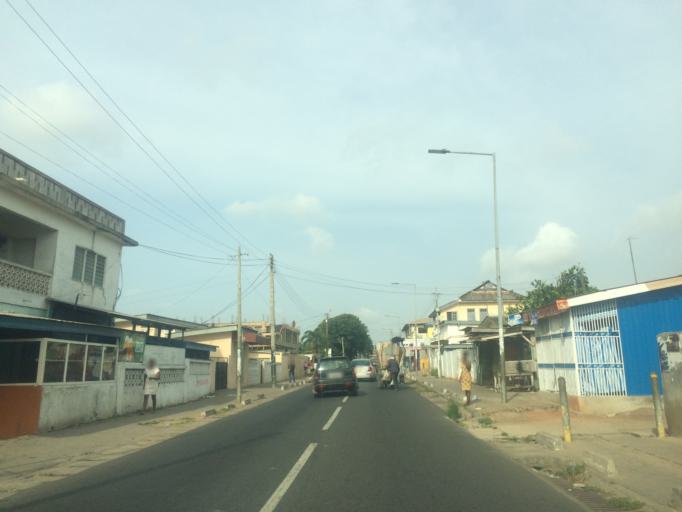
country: GH
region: Greater Accra
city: Accra
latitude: 5.5532
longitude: -0.1849
